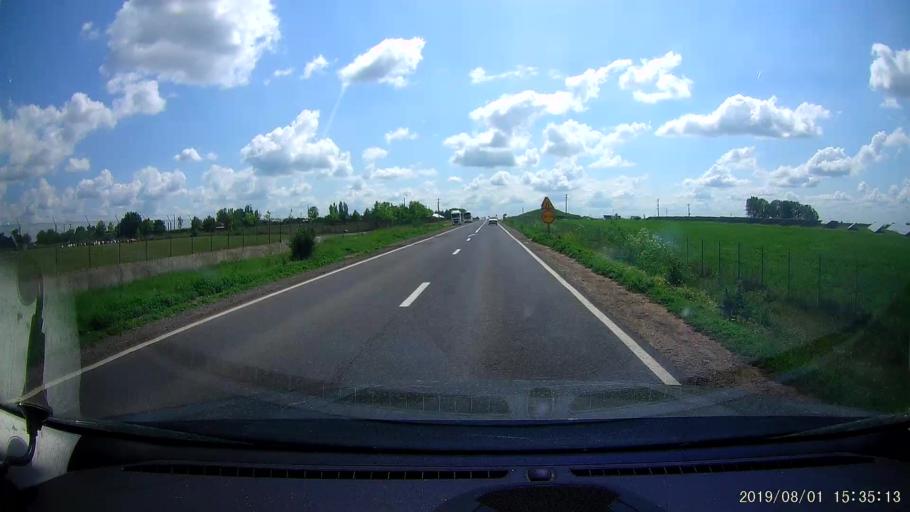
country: RO
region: Braila
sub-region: Comuna Insuratei
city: Insuratei
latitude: 44.9080
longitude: 27.5949
